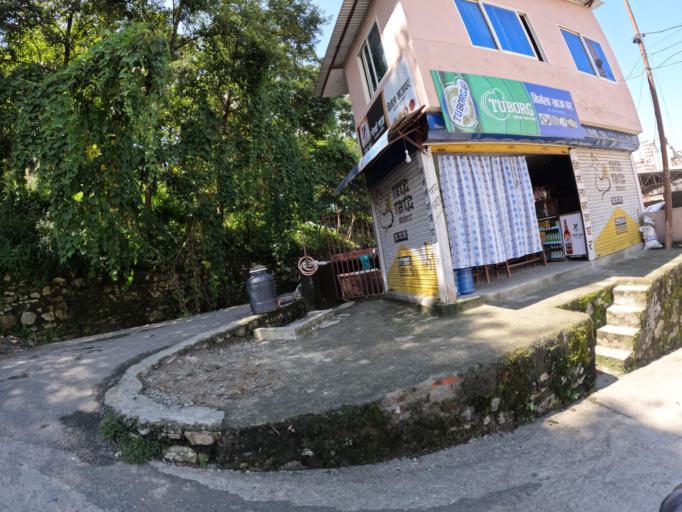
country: NP
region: Central Region
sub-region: Bagmati Zone
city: Kathmandu
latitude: 27.7546
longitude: 85.3299
